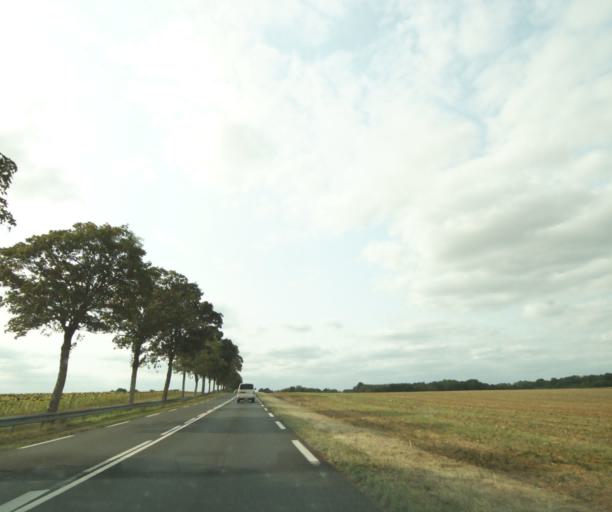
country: FR
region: Centre
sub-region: Departement d'Indre-et-Loire
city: Reignac-sur-Indre
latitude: 47.2279
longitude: 0.8789
